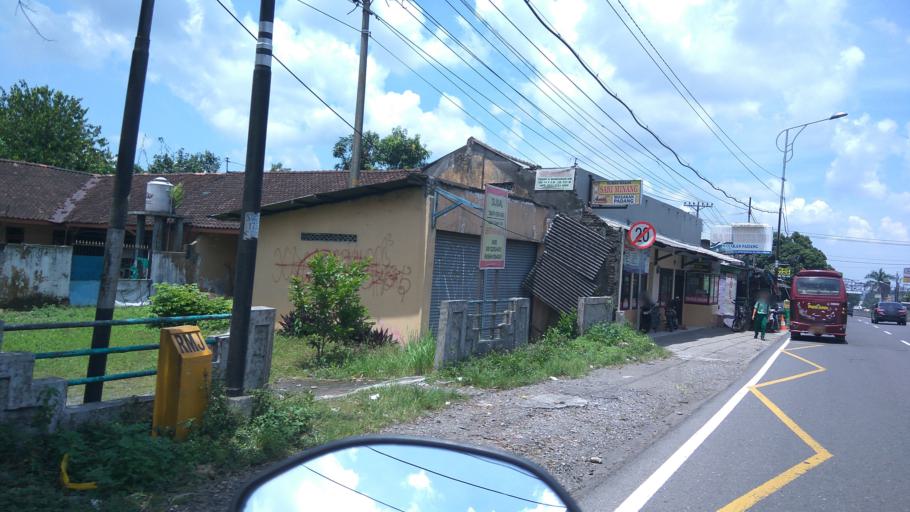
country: ID
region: Central Java
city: Ungaran
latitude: -7.1540
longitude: 110.4101
